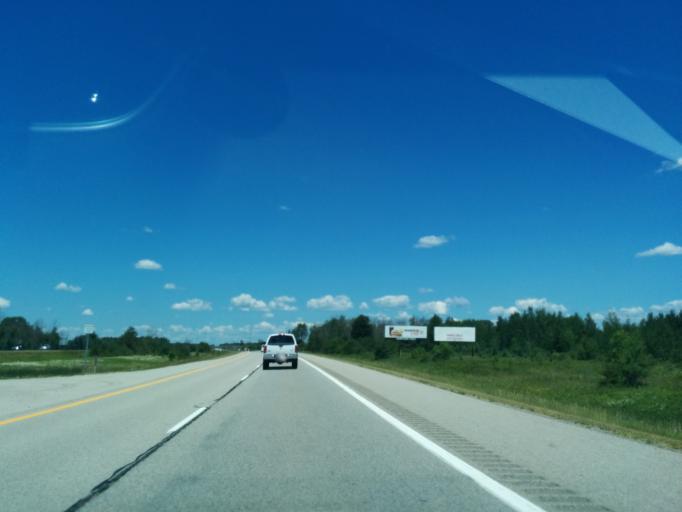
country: US
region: Michigan
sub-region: Ogemaw County
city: Skidway Lake
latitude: 44.1227
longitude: -84.1225
